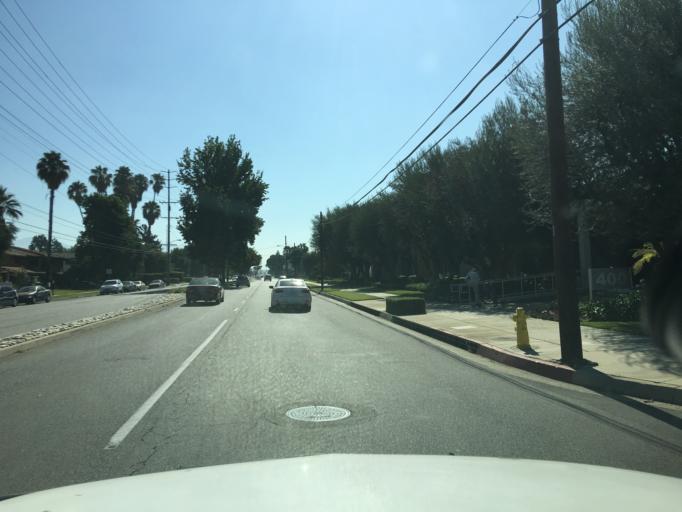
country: US
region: California
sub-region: Los Angeles County
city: North El Monte
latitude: 34.1086
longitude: -118.0217
